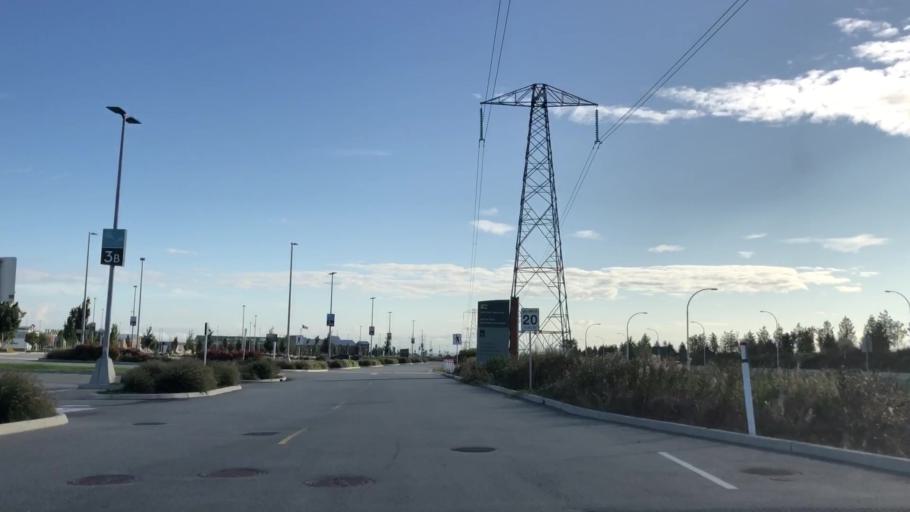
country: US
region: Washington
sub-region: Whatcom County
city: Point Roberts
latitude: 49.0340
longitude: -123.0881
